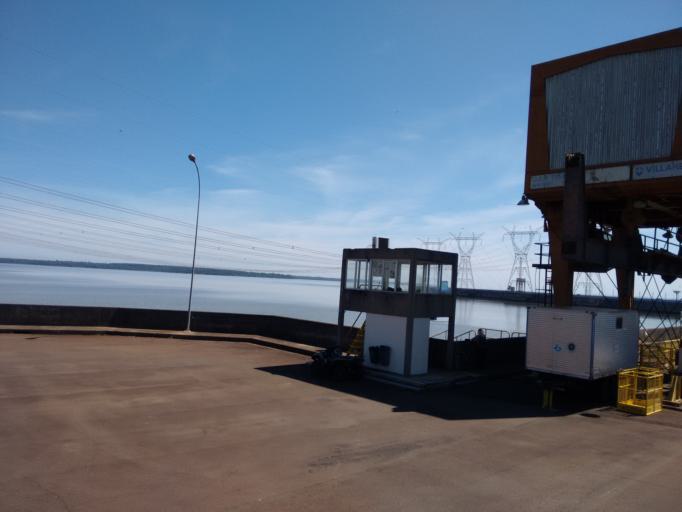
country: PY
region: Alto Parana
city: Ciudad del Este
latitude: -25.4149
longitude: -54.6006
